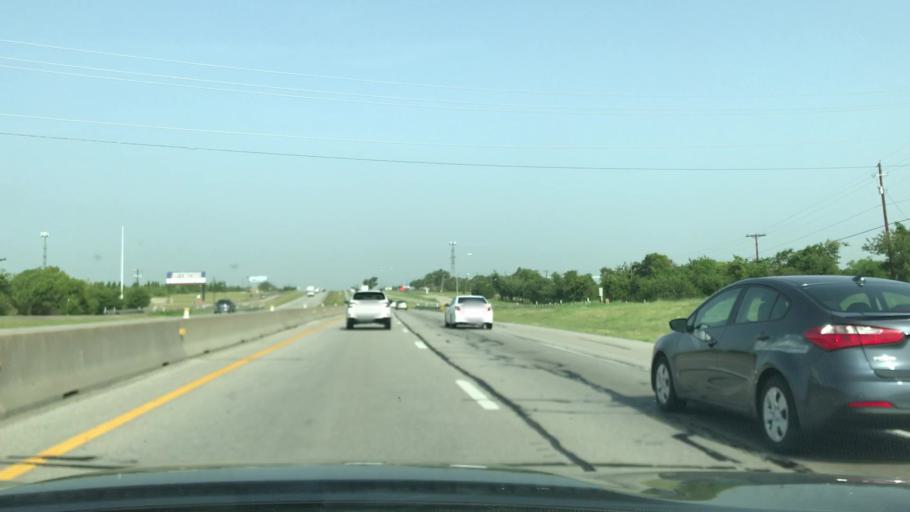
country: US
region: Texas
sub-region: Dallas County
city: Sunnyvale
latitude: 32.7858
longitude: -96.5671
